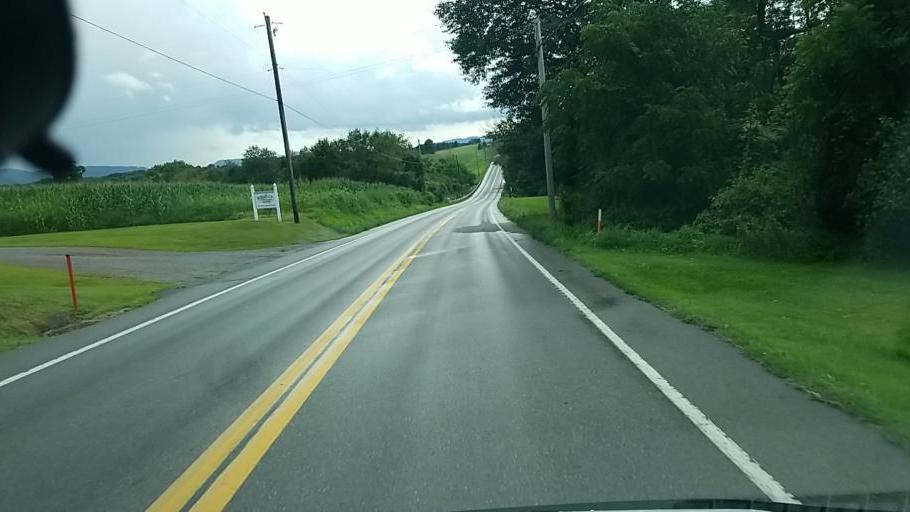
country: US
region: Pennsylvania
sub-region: Dauphin County
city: Elizabethville
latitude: 40.5783
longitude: -76.8856
